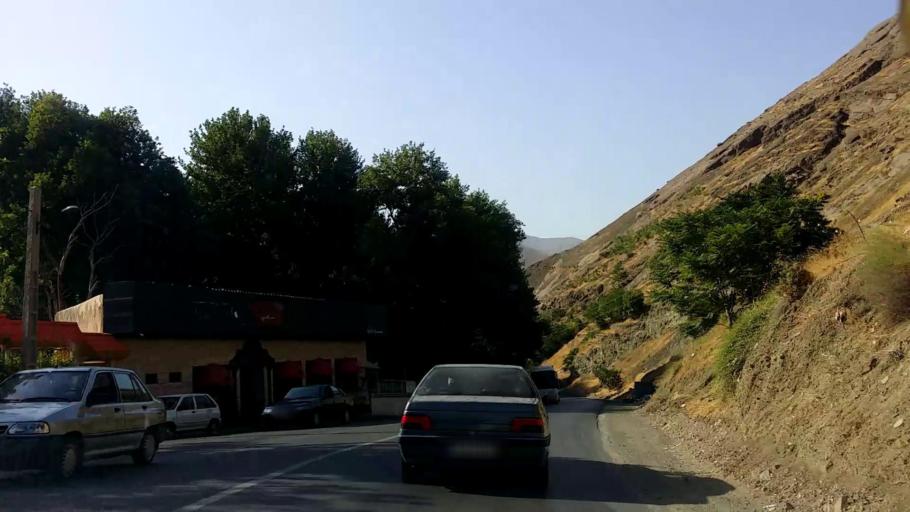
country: IR
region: Alborz
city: Karaj
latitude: 35.8614
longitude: 51.0559
